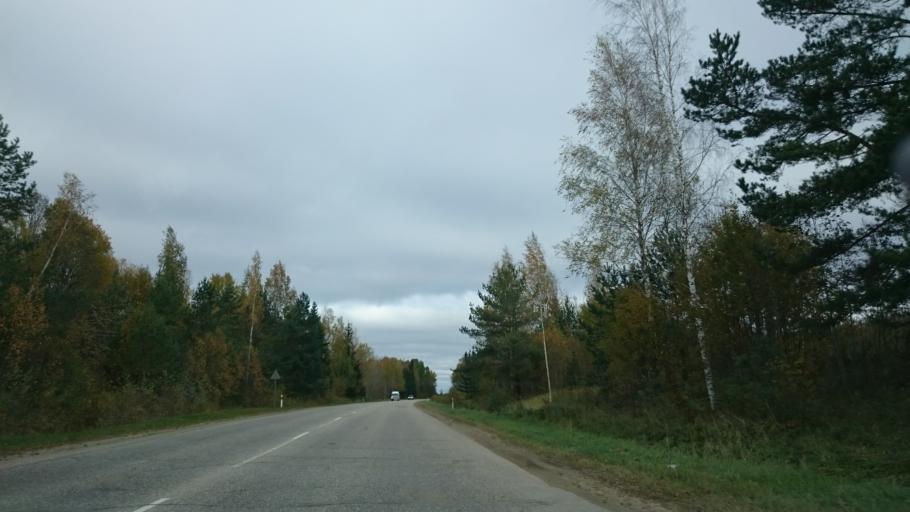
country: LV
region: Amatas Novads
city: Drabesi
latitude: 57.2367
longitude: 25.2537
